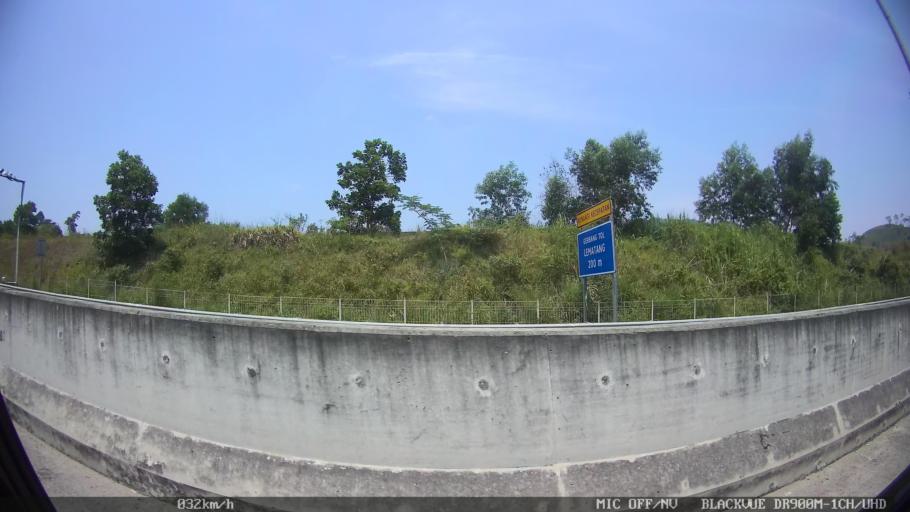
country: ID
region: Lampung
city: Panjang
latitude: -5.4074
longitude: 105.3468
